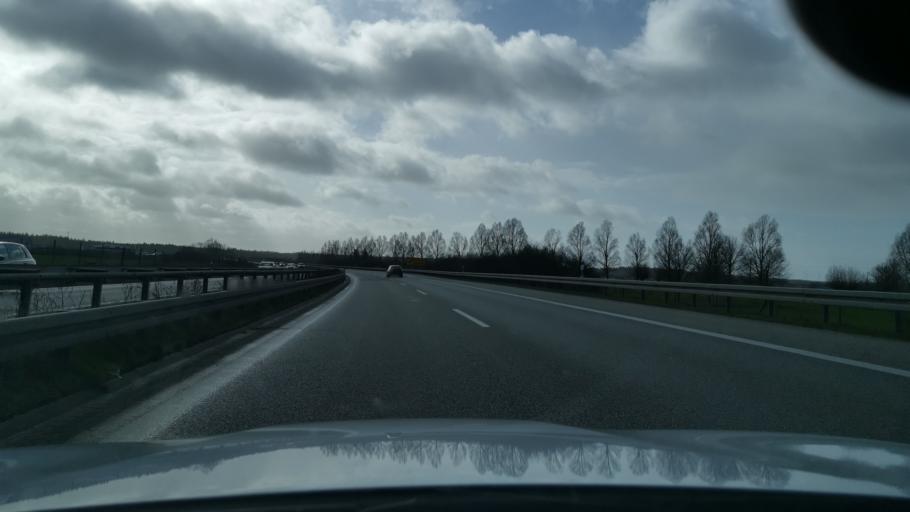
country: DE
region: Mecklenburg-Vorpommern
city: Stabelow
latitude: 54.0500
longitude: 12.0330
